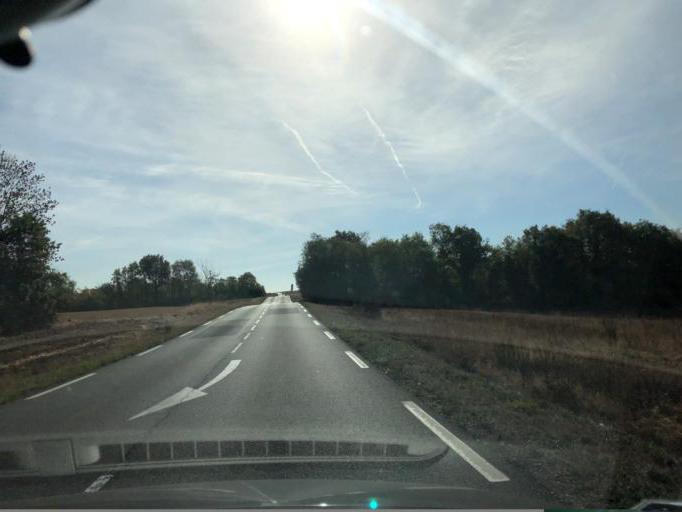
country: FR
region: Centre
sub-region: Departement du Loiret
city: Sermaises
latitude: 48.3655
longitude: 2.2530
